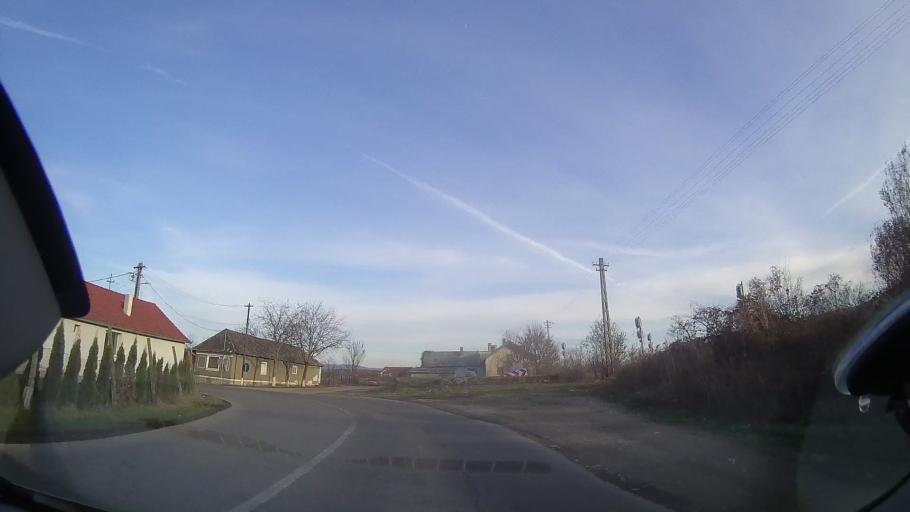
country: RO
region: Bihor
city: Lugasu de Jos
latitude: 47.0404
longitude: 22.3525
